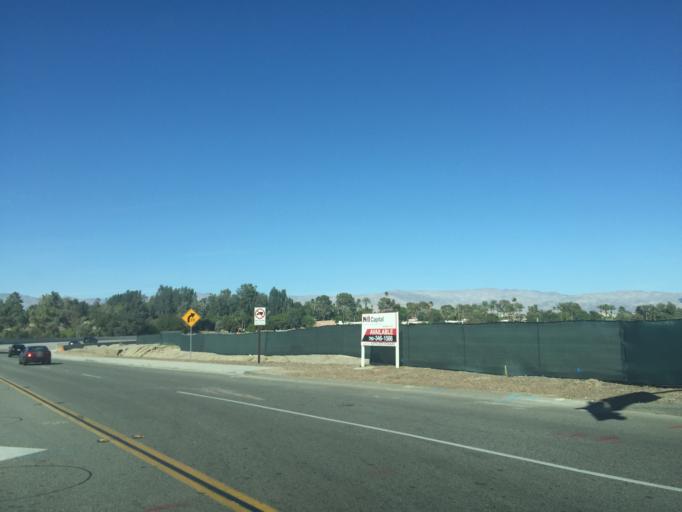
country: US
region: California
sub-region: Riverside County
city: Indian Wells
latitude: 33.7211
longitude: -116.3177
